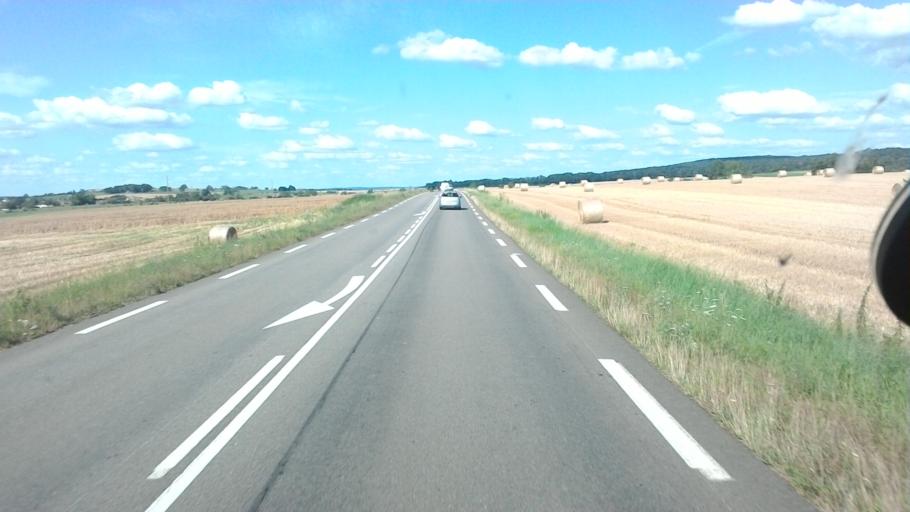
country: FR
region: Franche-Comte
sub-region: Departement de la Haute-Saone
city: Gy
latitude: 47.4490
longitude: 5.8904
